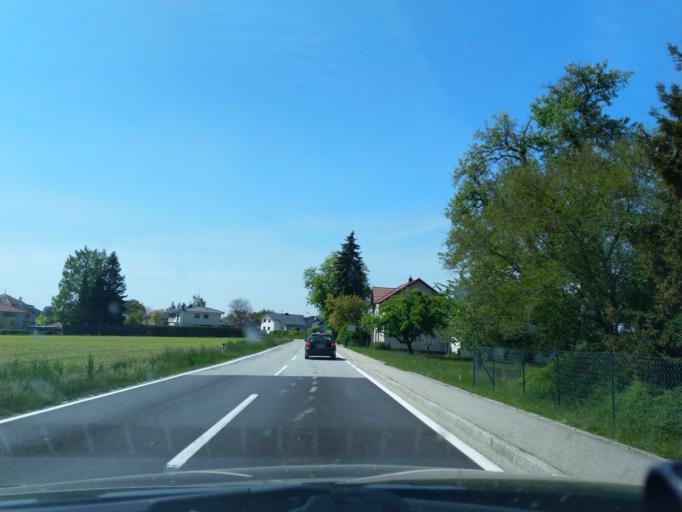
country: DE
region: Bavaria
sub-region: Lower Bavaria
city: Bad Fussing
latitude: 48.2768
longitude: 13.3779
